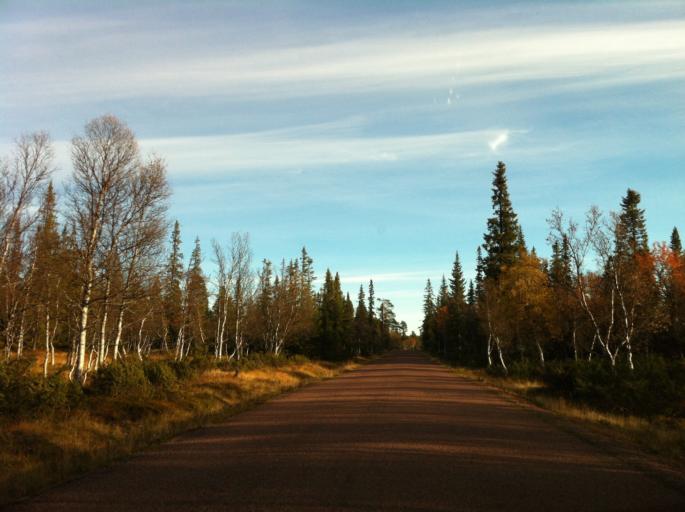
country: NO
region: Hedmark
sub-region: Engerdal
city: Engerdal
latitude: 62.0787
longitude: 12.1649
